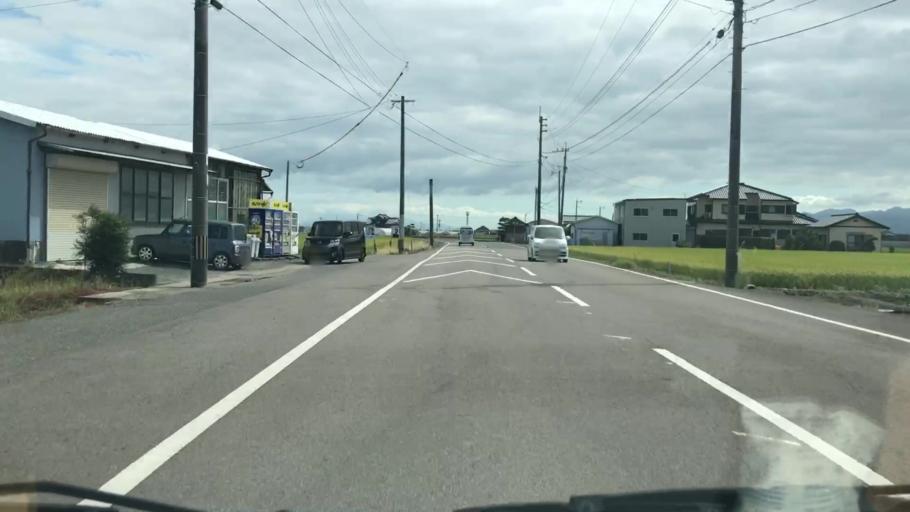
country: JP
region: Saga Prefecture
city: Saga-shi
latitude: 33.1978
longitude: 130.1814
